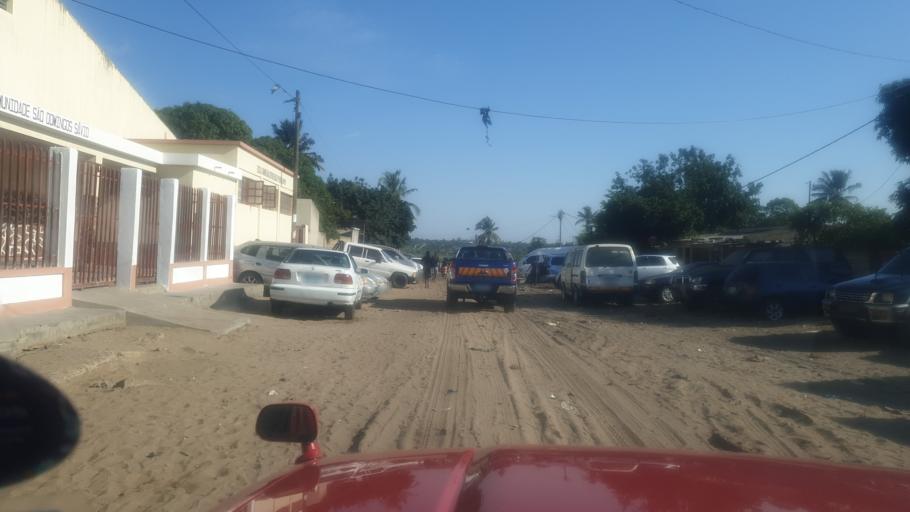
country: MZ
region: Maputo City
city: Maputo
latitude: -25.9179
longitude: 32.5552
